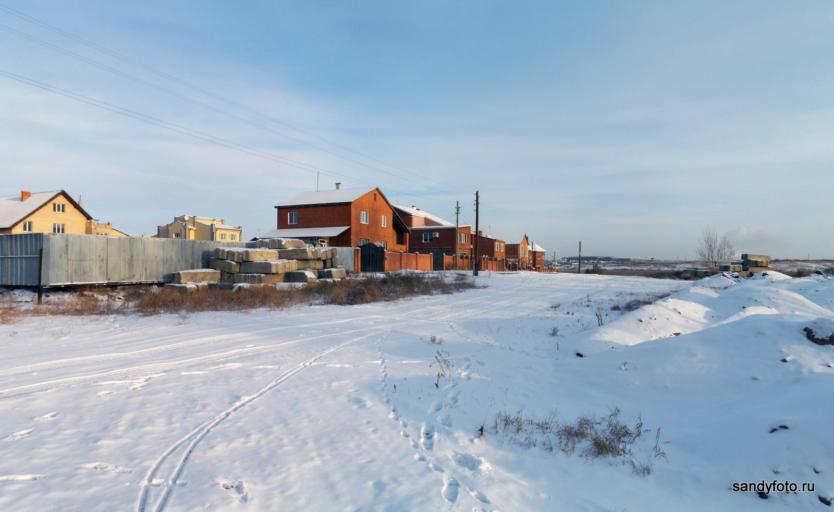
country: RU
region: Chelyabinsk
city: Troitsk
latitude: 54.0686
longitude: 61.5344
